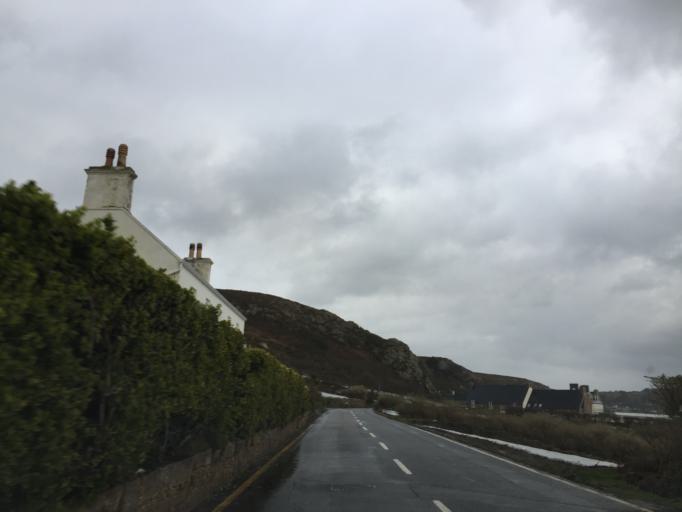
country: JE
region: St Helier
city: Saint Helier
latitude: 49.2412
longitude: -2.2471
